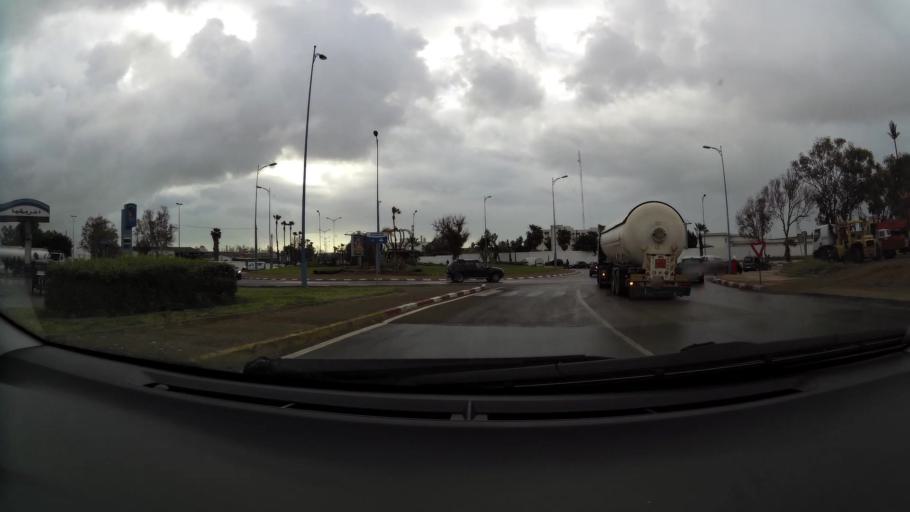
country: MA
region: Grand Casablanca
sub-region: Mohammedia
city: Mohammedia
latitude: 33.6820
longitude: -7.4063
